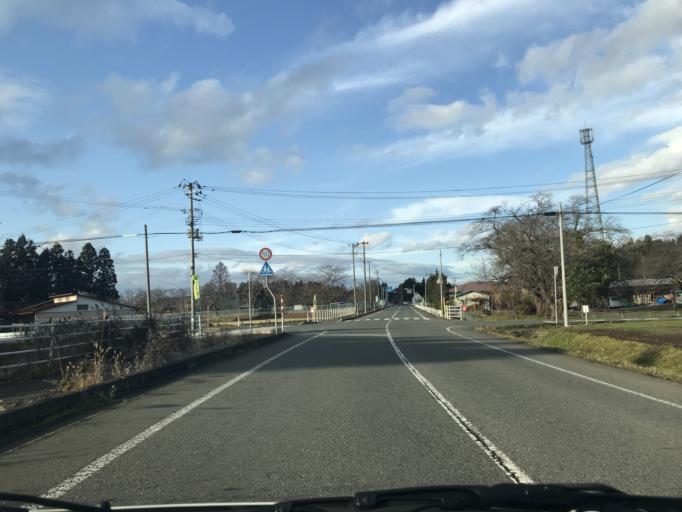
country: JP
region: Iwate
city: Mizusawa
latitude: 39.1949
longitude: 141.0698
